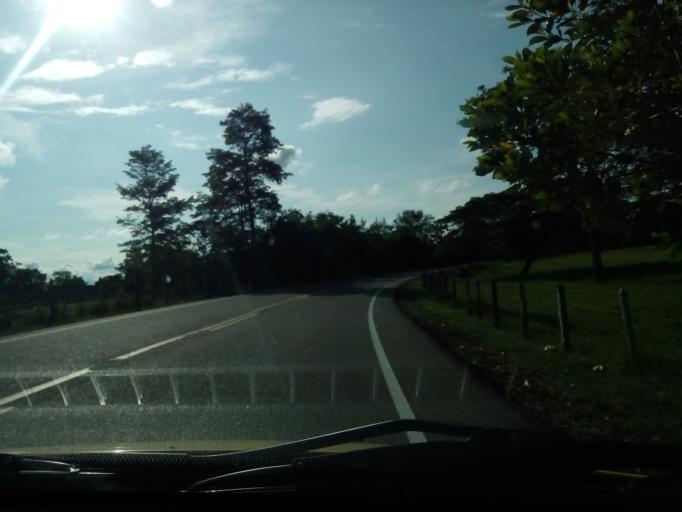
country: CO
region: Boyaca
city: Puerto Boyaca
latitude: 5.9322
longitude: -74.5354
